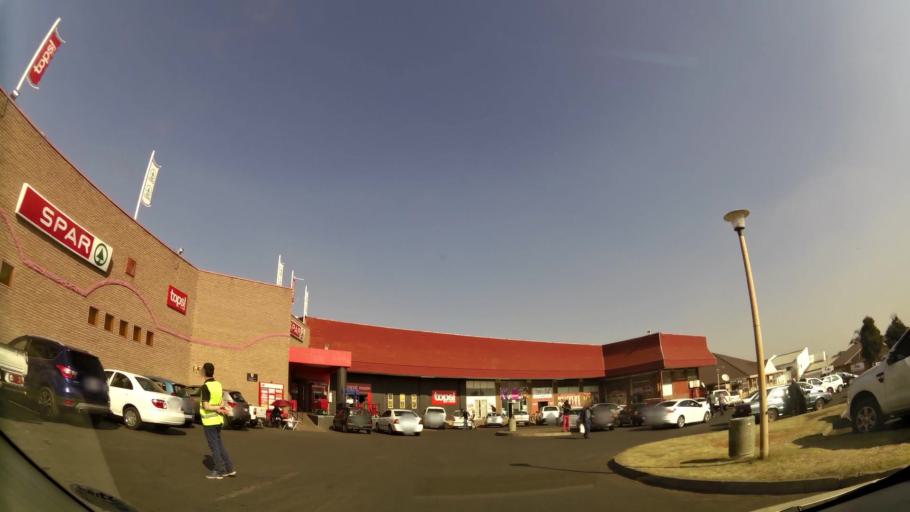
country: ZA
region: Gauteng
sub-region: West Rand District Municipality
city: Randfontein
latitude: -26.1665
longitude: 27.6989
